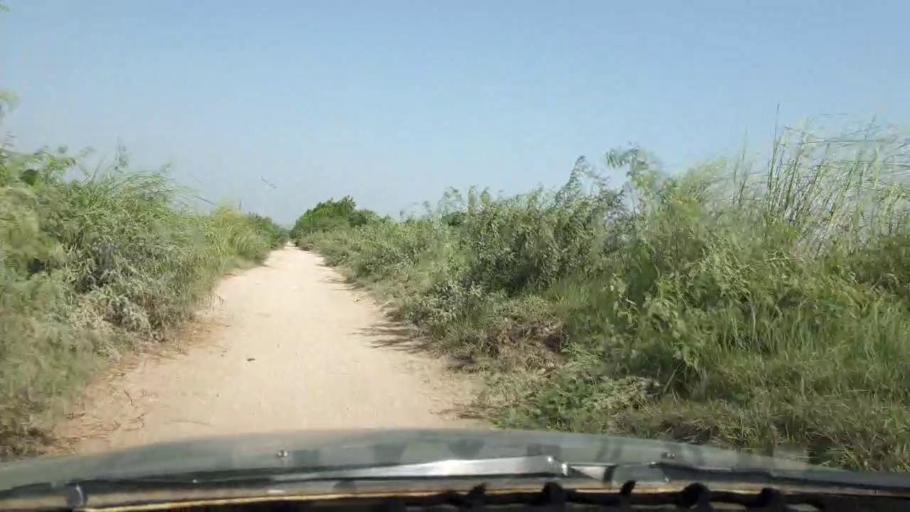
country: PK
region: Sindh
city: Matli
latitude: 25.0816
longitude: 68.6146
